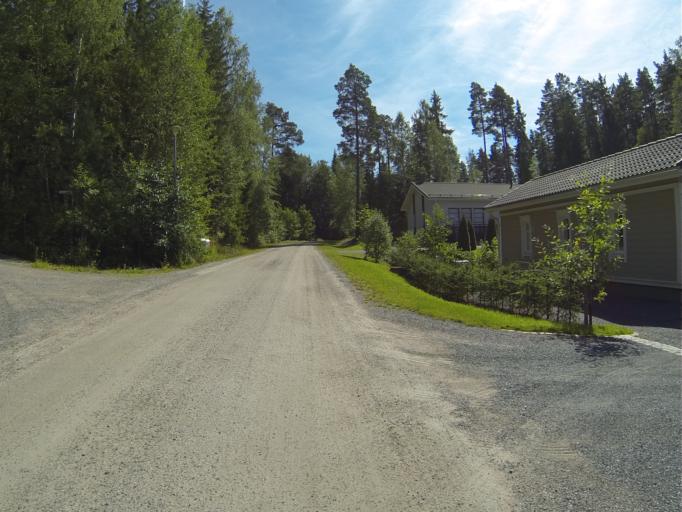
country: FI
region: Varsinais-Suomi
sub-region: Salo
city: Saerkisalo
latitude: 60.2582
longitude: 22.9701
